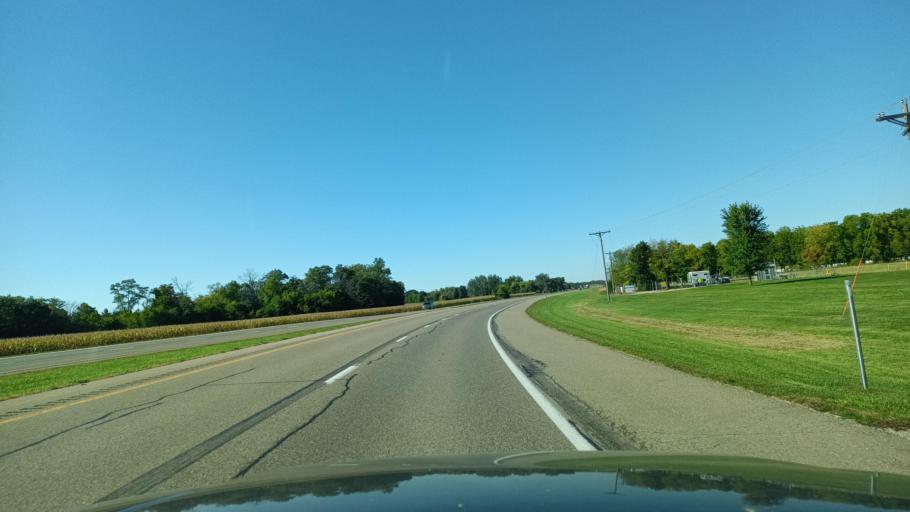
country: US
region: Iowa
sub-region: Lee County
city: Fort Madison
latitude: 40.6807
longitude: -91.2527
